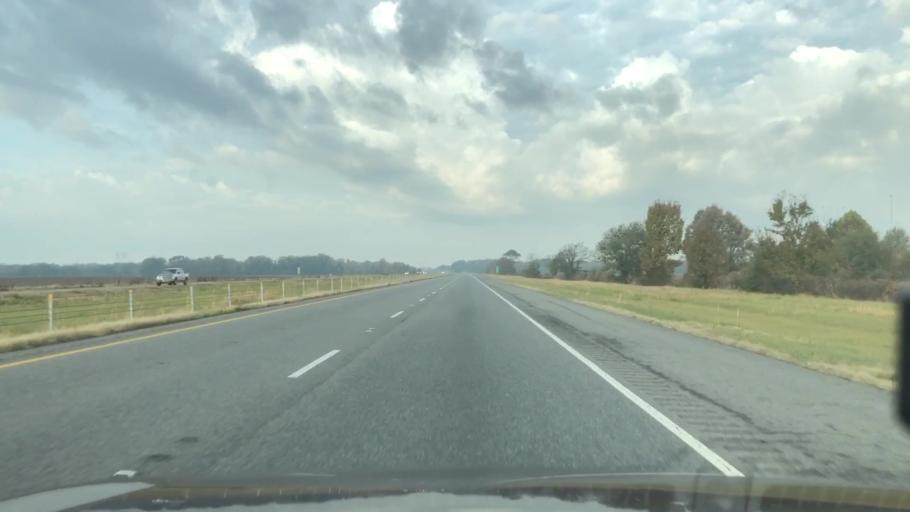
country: US
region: Louisiana
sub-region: Madison Parish
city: Tallulah
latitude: 32.4164
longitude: -91.2816
